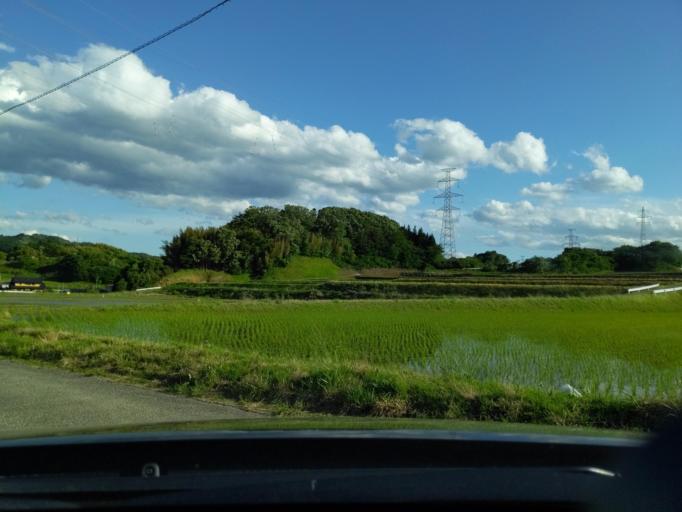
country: JP
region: Fukushima
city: Miharu
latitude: 37.4013
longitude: 140.4506
